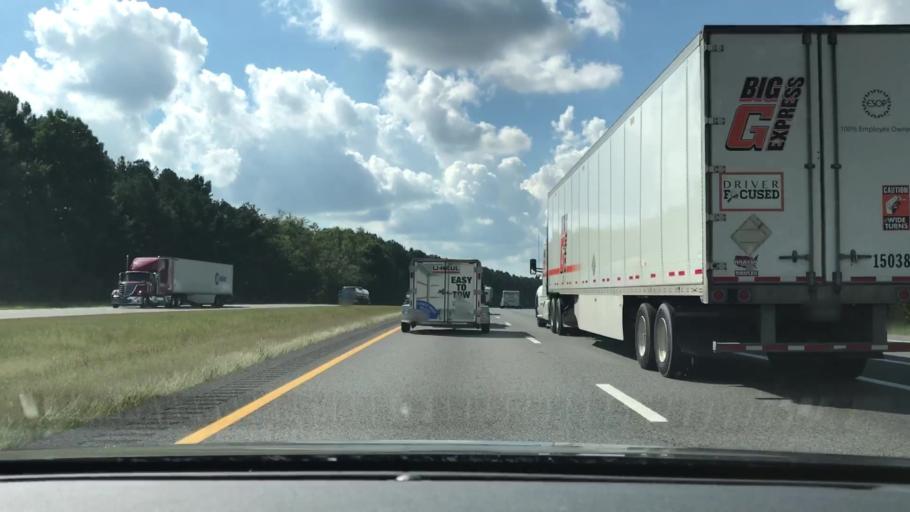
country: US
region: Tennessee
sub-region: Sumner County
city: White House
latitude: 36.5238
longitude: -86.6446
